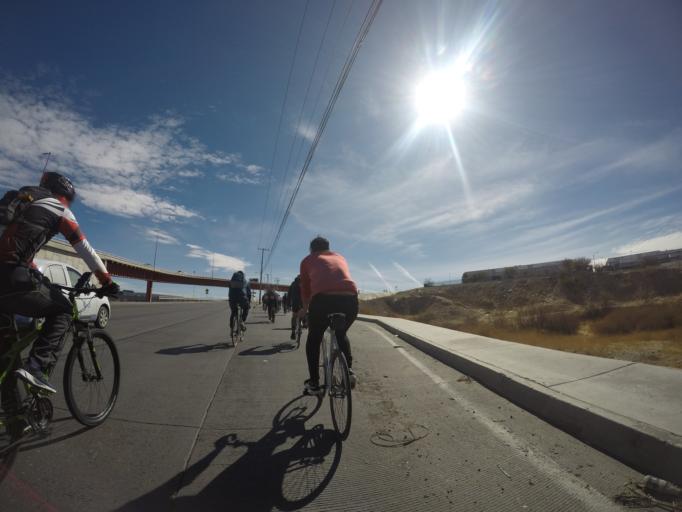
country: US
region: Texas
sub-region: El Paso County
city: Socorro
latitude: 31.6710
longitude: -106.4024
